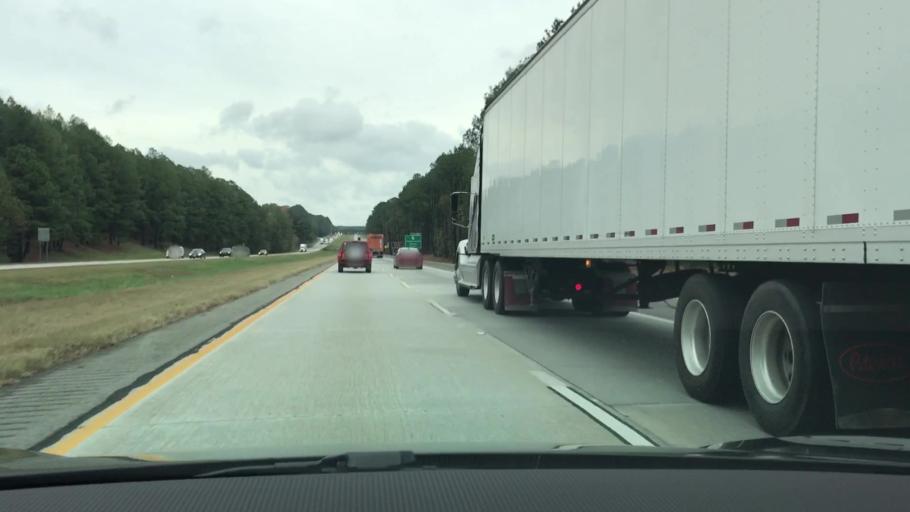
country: US
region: Georgia
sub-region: Taliaferro County
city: Crawfordville
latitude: 33.5303
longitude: -82.9253
